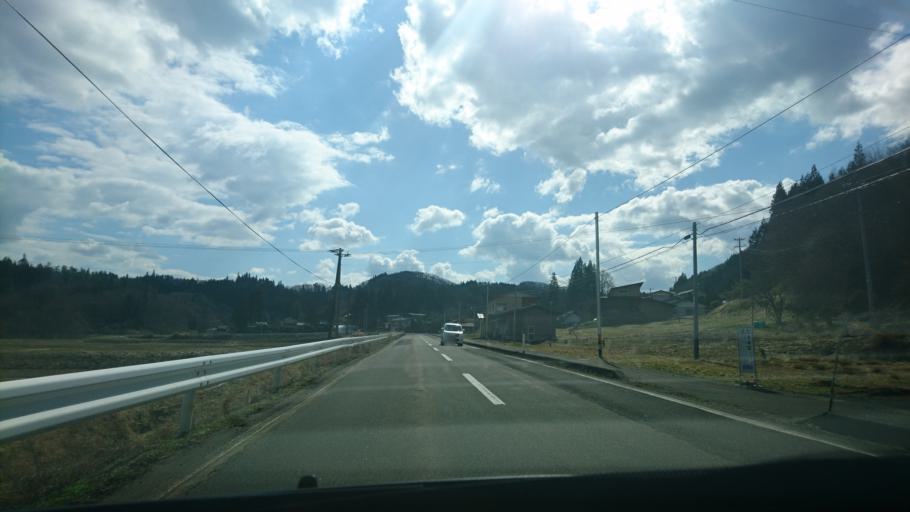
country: JP
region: Iwate
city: Hanamaki
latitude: 39.3440
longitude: 141.2379
